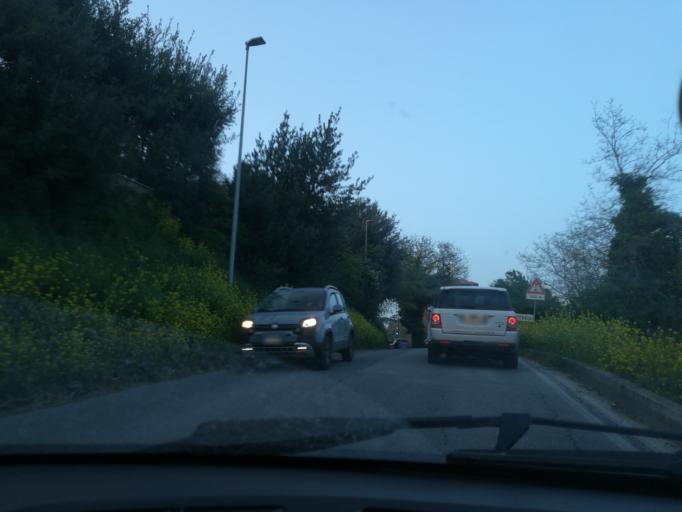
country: IT
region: The Marches
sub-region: Provincia di Macerata
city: Macerata
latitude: 43.2855
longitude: 13.4507
